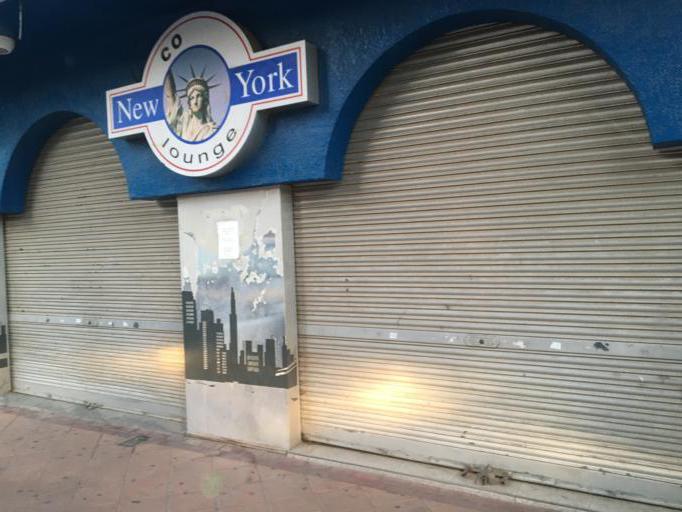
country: ES
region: Murcia
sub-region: Murcia
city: Murcia
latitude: 37.9809
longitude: -1.1194
